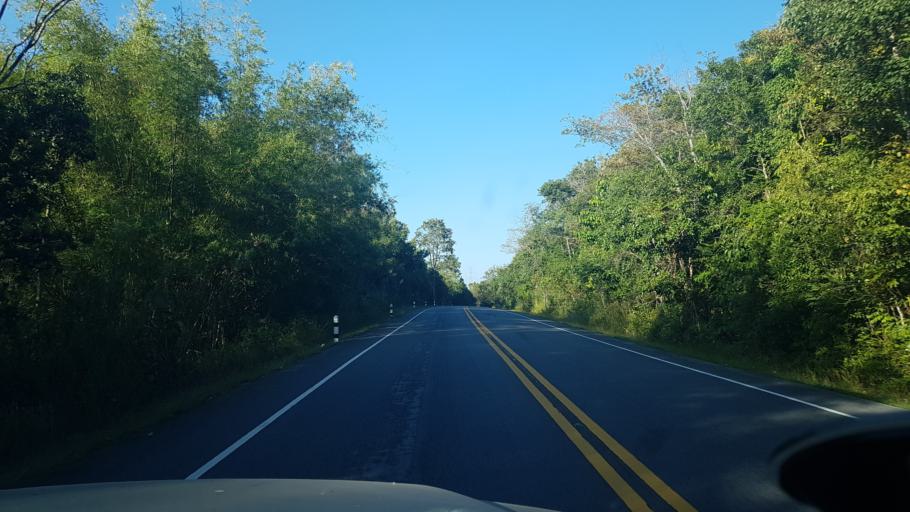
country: TH
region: Phetchabun
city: Nam Nao
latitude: 16.6963
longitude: 101.6379
